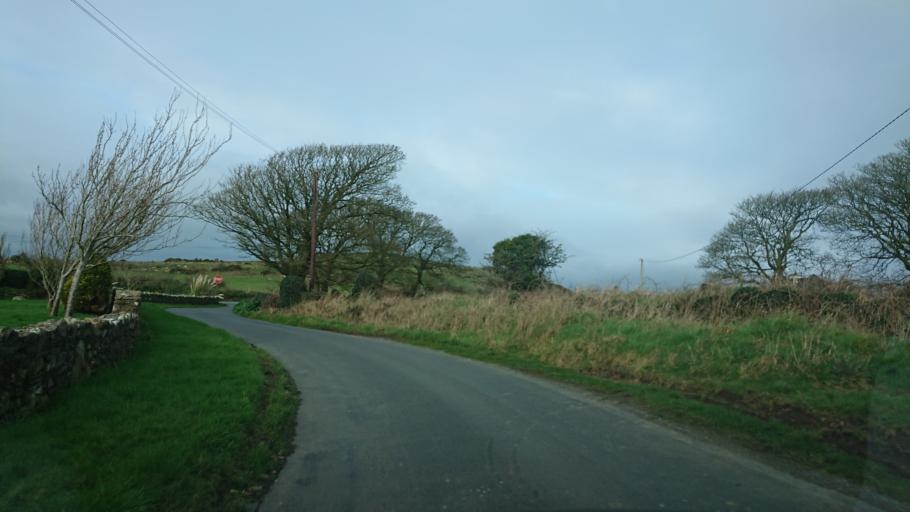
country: IE
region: Munster
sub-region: Waterford
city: Tra Mhor
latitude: 52.1632
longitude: -7.2150
